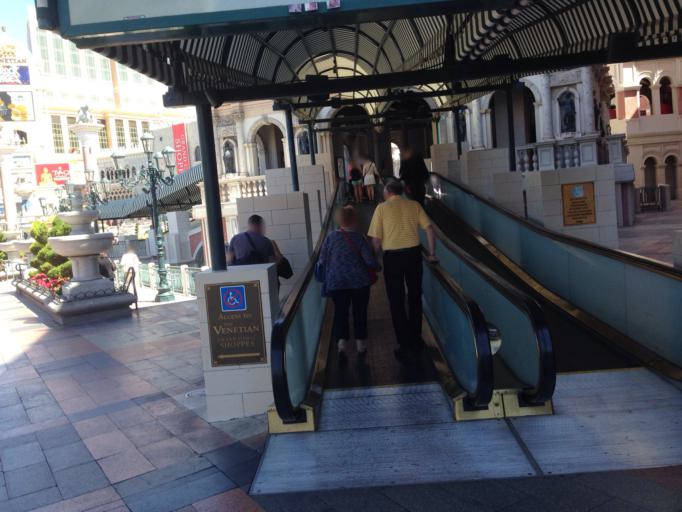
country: US
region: Nevada
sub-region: Clark County
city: Paradise
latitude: 36.1214
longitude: -115.1717
